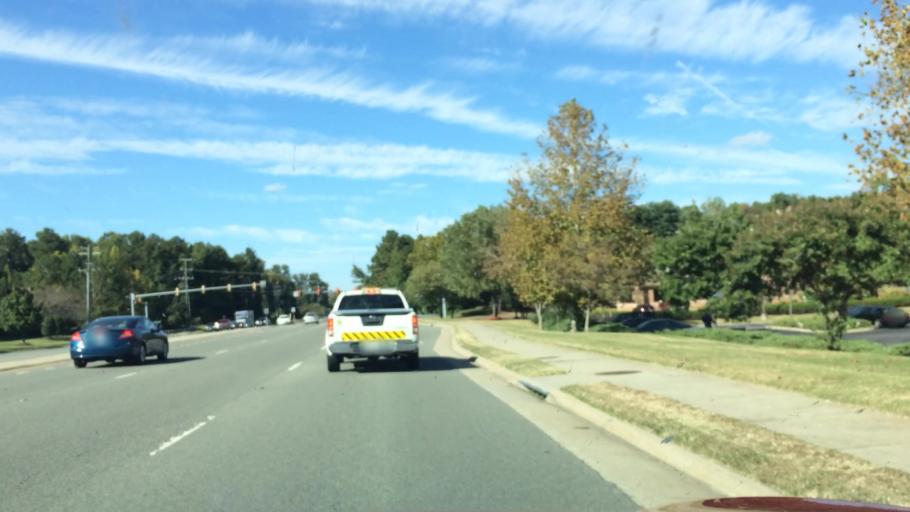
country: US
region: Virginia
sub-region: Henrico County
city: Glen Allen
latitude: 37.6749
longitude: -77.4608
